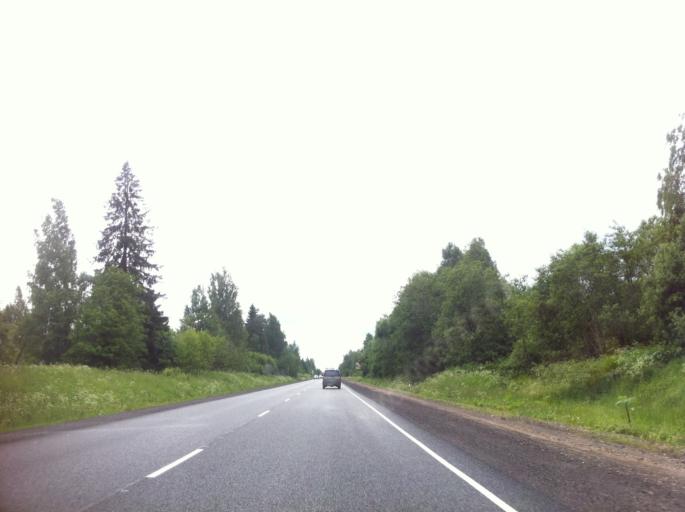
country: RU
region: Leningrad
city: Rozhdestveno
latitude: 59.2402
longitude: 29.9299
